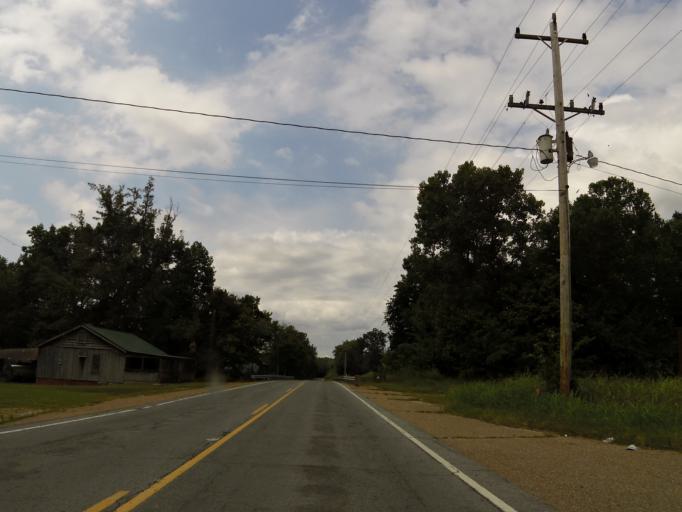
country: US
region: Tennessee
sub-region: Perry County
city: Linden
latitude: 35.6198
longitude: -87.9547
